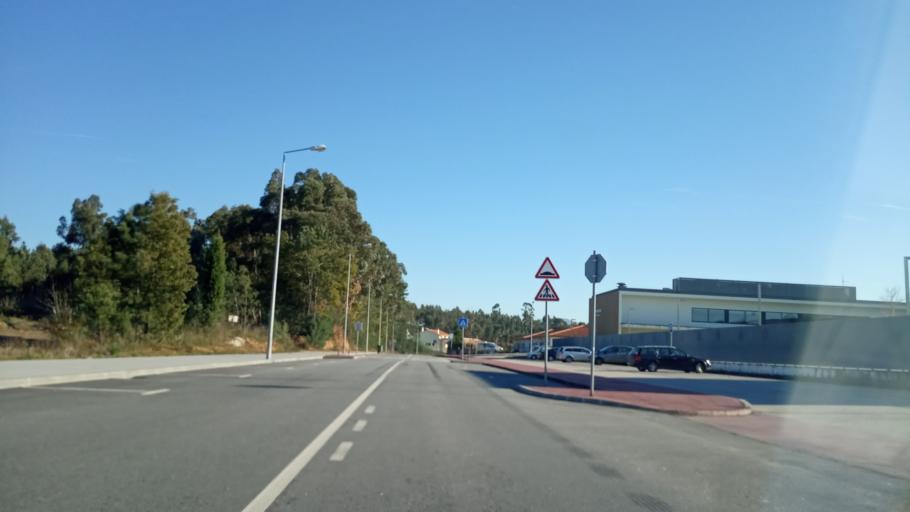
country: PT
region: Aveiro
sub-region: Anadia
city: Anadia
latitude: 40.4340
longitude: -8.4391
